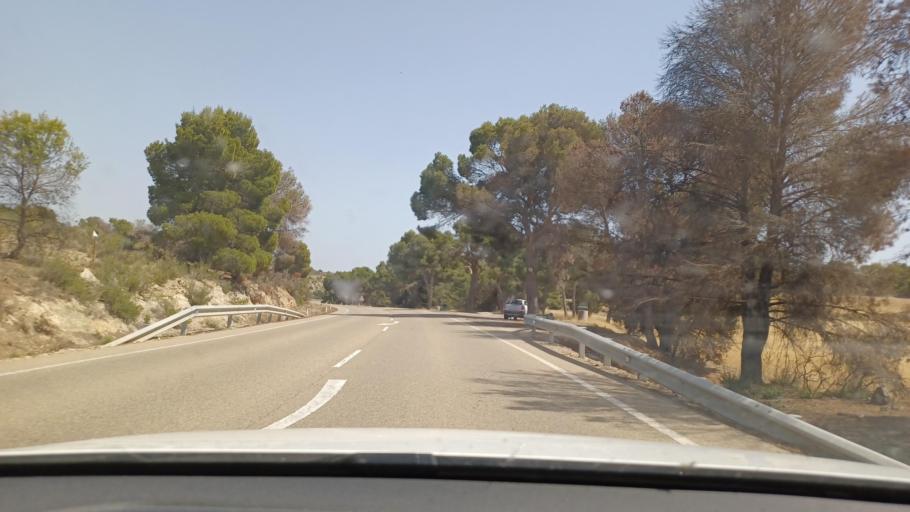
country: ES
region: Aragon
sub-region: Provincia de Zaragoza
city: Chiprana
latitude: 41.3623
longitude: -0.1058
